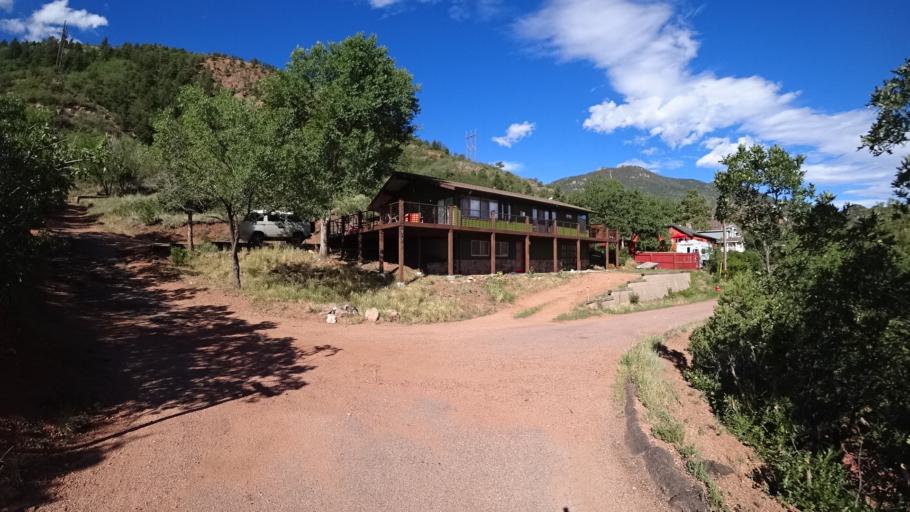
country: US
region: Colorado
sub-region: El Paso County
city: Manitou Springs
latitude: 38.8549
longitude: -104.9189
